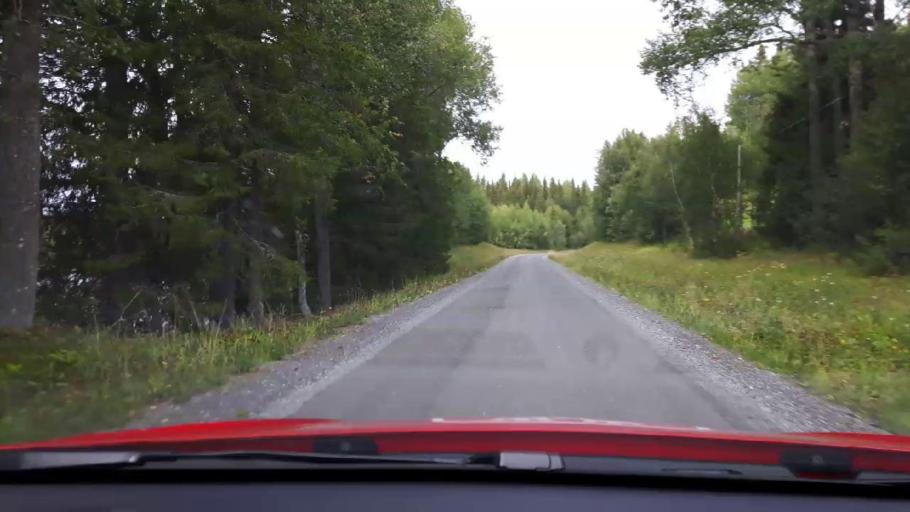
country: SE
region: Jaemtland
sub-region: Are Kommun
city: Are
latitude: 63.7485
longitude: 13.0884
